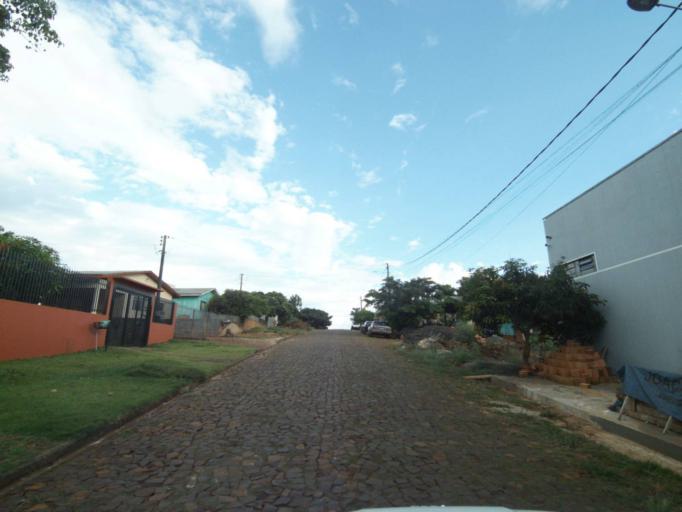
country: BR
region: Parana
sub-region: Laranjeiras Do Sul
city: Laranjeiras do Sul
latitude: -25.4881
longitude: -52.5244
